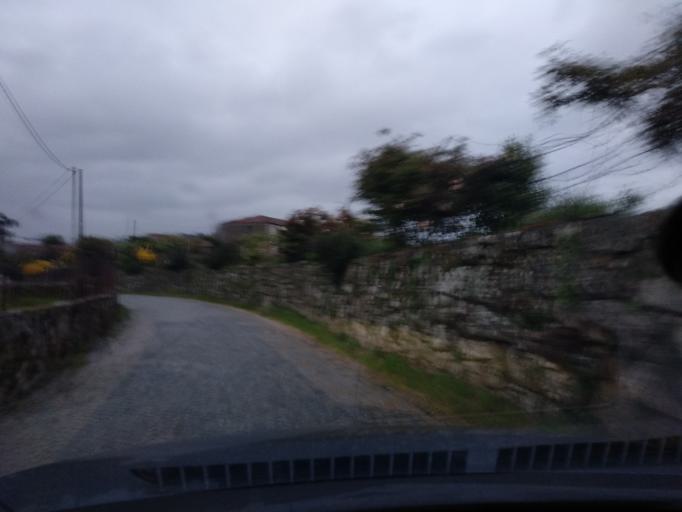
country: PT
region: Porto
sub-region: Penafiel
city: Penafiel
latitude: 41.1865
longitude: -8.2946
